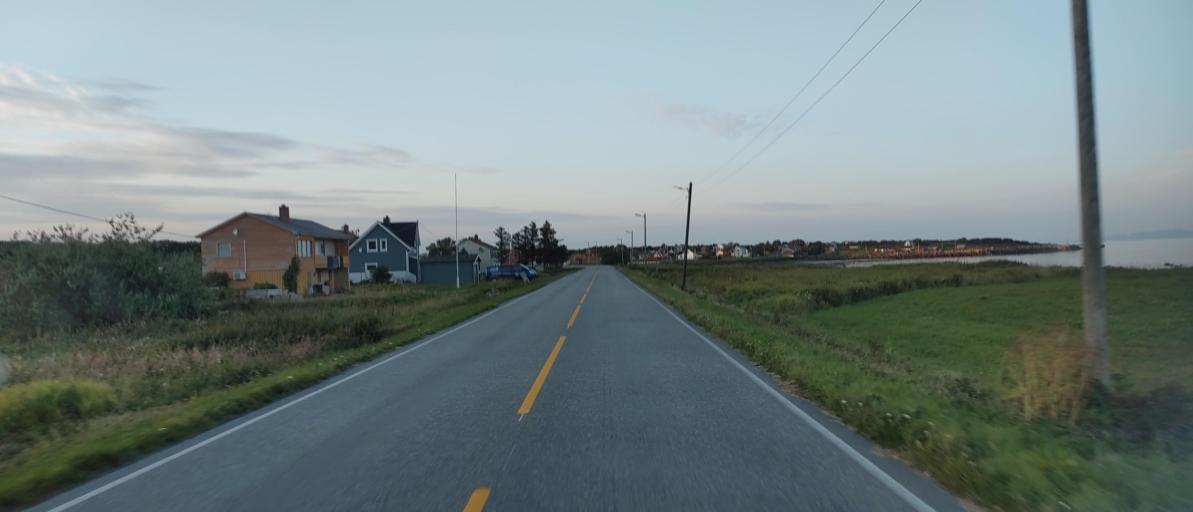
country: NO
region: Nordland
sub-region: Andoy
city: Andenes
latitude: 69.2421
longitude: 16.1160
